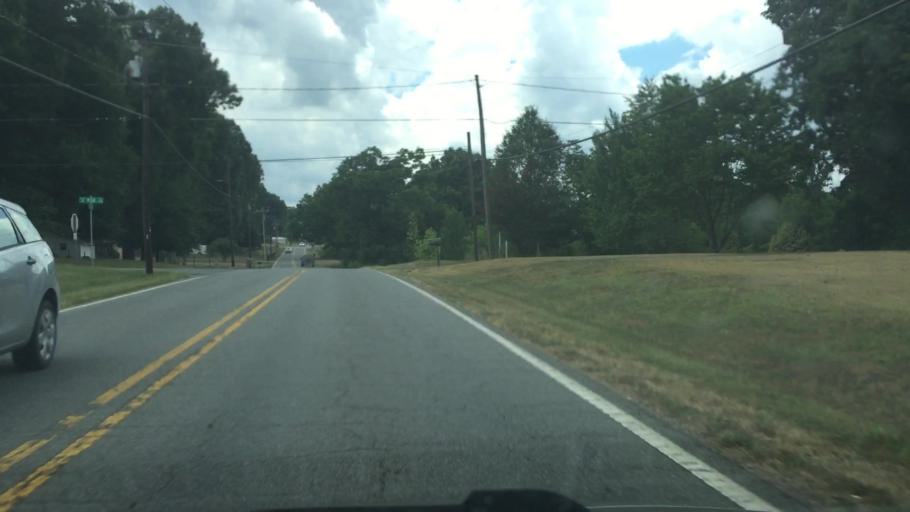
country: US
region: North Carolina
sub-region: Rowan County
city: Enochville
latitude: 35.5218
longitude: -80.6698
